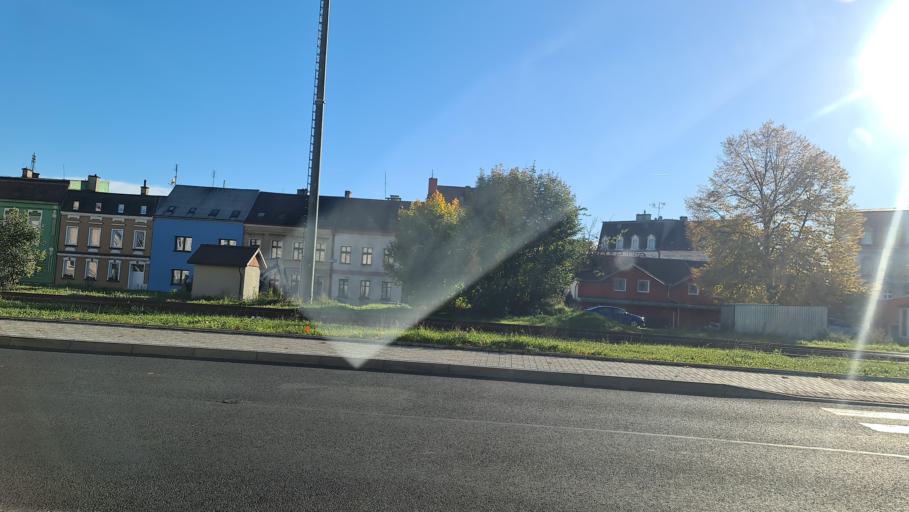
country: CZ
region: Karlovarsky
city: As
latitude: 50.2196
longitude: 12.1822
